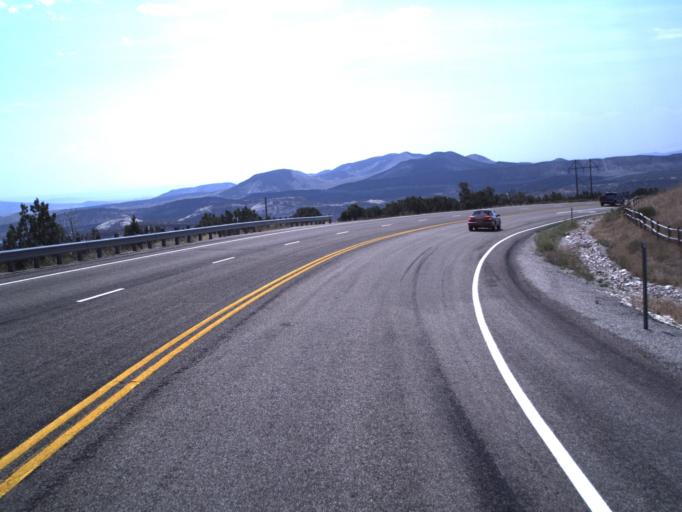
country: US
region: Utah
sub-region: Uintah County
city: Vernal
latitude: 40.6235
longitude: -109.4732
